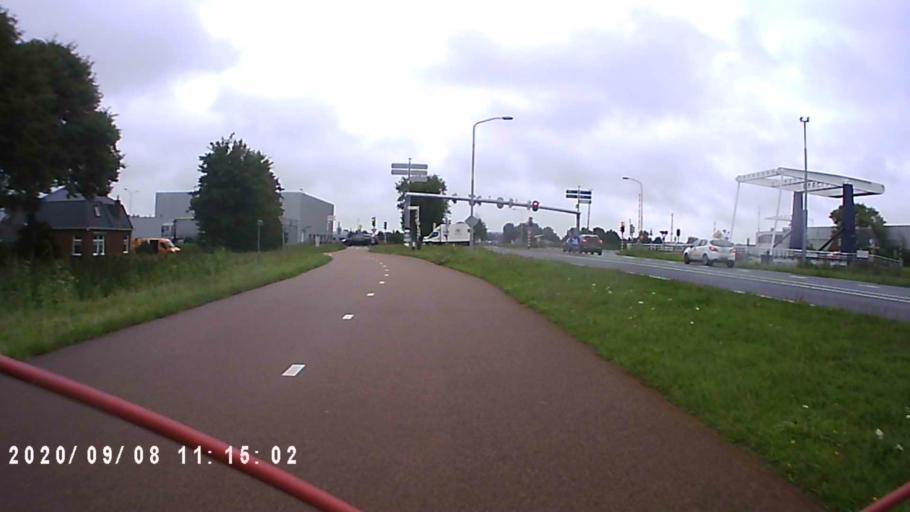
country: NL
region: Groningen
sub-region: Gemeente Hoogezand-Sappemeer
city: Hoogezand
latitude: 53.1719
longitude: 6.7278
